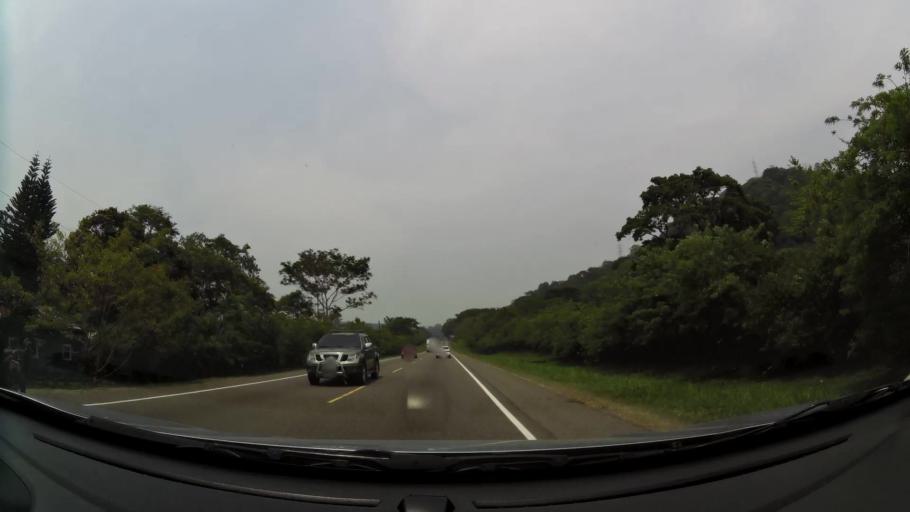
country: HN
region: Cortes
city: La Guama
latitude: 14.8754
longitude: -87.9445
